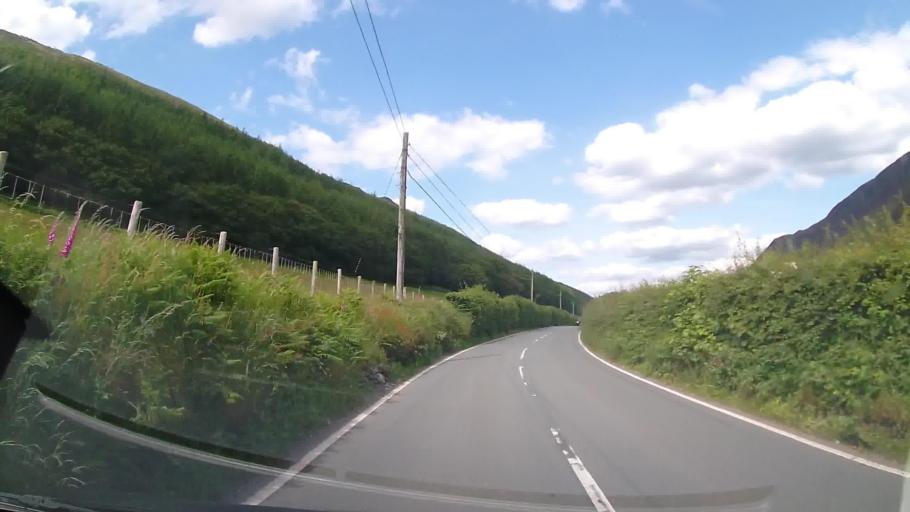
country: GB
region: Wales
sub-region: Gwynedd
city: Corris
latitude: 52.6561
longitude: -3.9337
